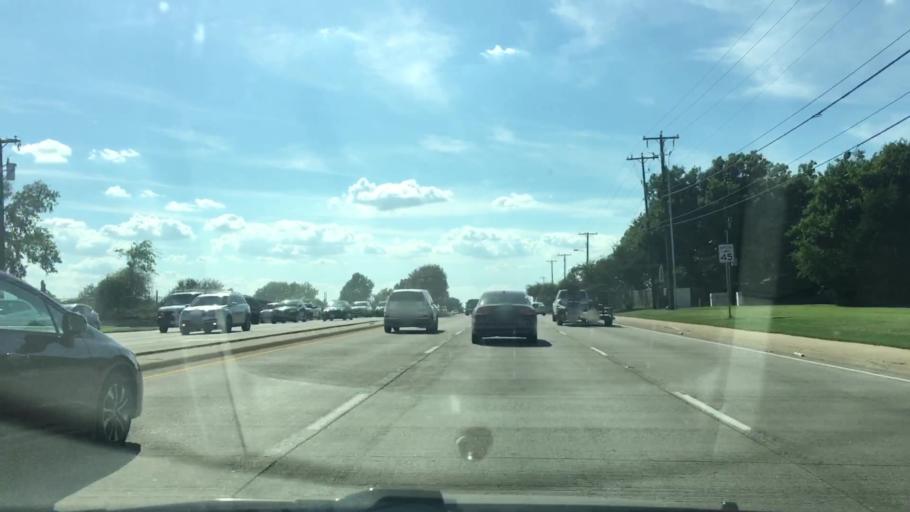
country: US
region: Texas
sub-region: Collin County
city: McKinney
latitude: 33.2170
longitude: -96.6445
